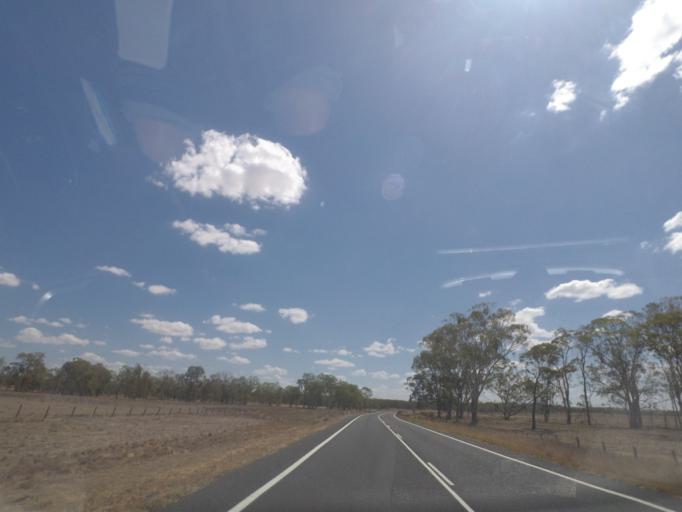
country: AU
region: Queensland
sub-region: Southern Downs
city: Warwick
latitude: -28.1824
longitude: 151.8184
